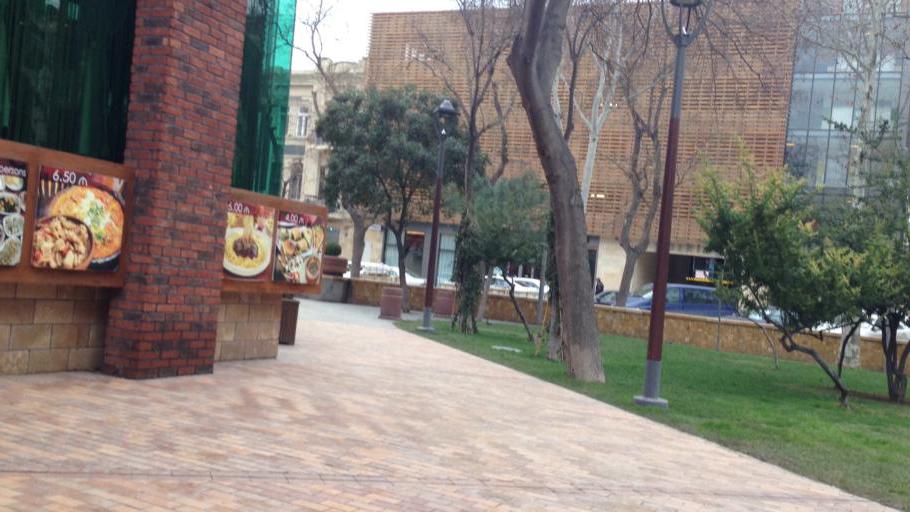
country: AZ
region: Baki
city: Badamdar
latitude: 40.3715
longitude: 49.8406
